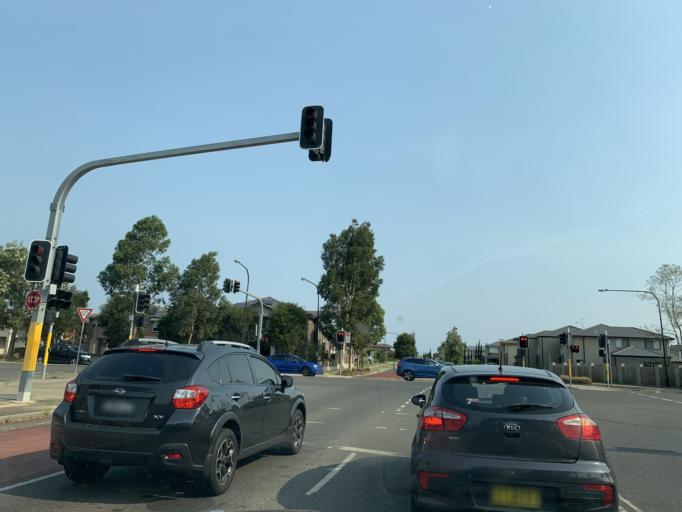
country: AU
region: New South Wales
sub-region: Blacktown
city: Quakers Hill
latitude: -33.7127
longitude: 150.8993
